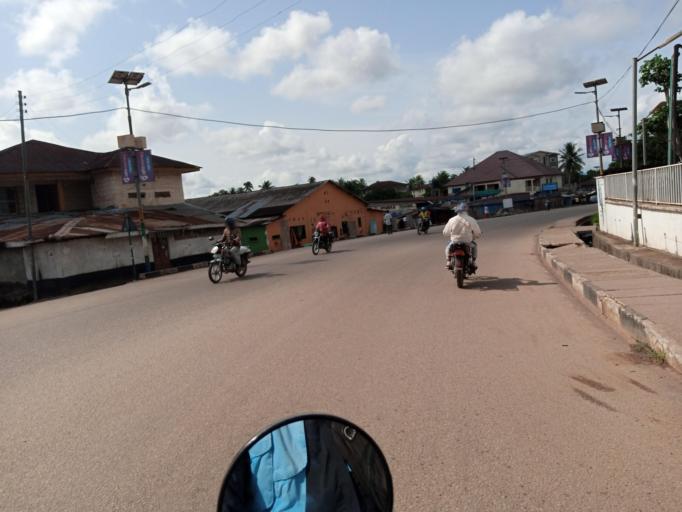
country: SL
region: Southern Province
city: Bo
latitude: 7.9615
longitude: -11.7402
